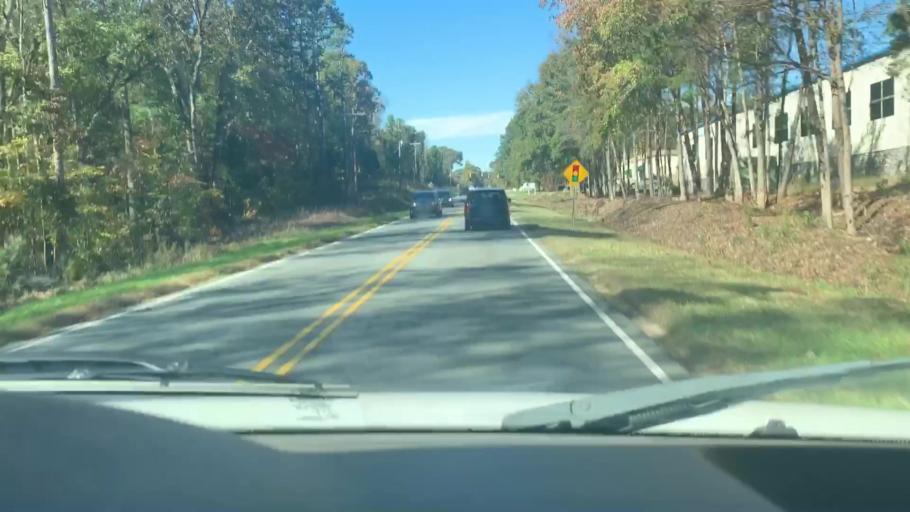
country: US
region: North Carolina
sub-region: Lincoln County
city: Lowesville
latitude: 35.4339
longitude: -80.9706
